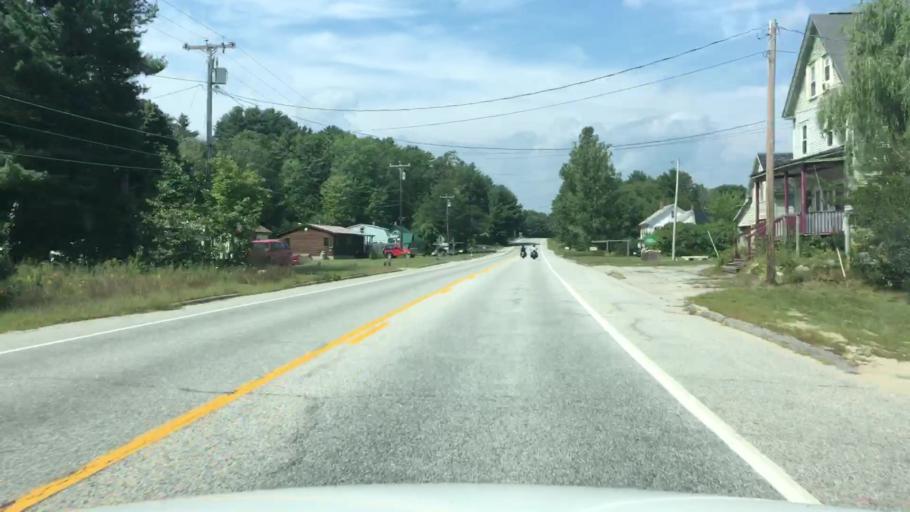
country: US
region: Maine
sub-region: Oxford County
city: Peru
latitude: 44.4878
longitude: -70.3789
